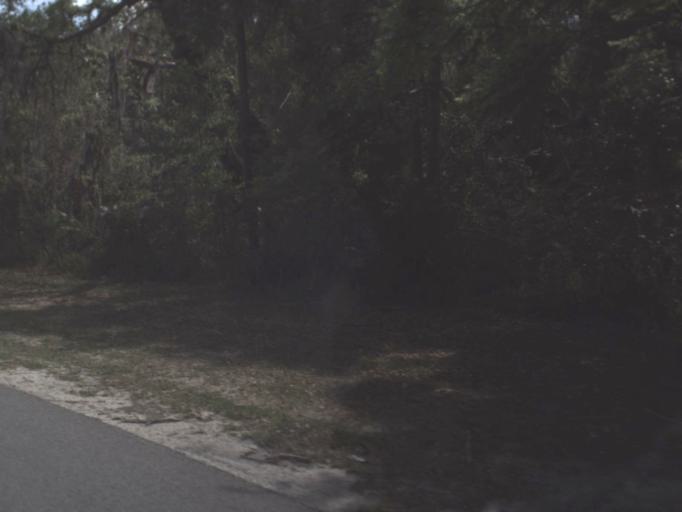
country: US
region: Florida
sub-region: Flagler County
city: Palm Coast
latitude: 29.5956
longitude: -81.1951
